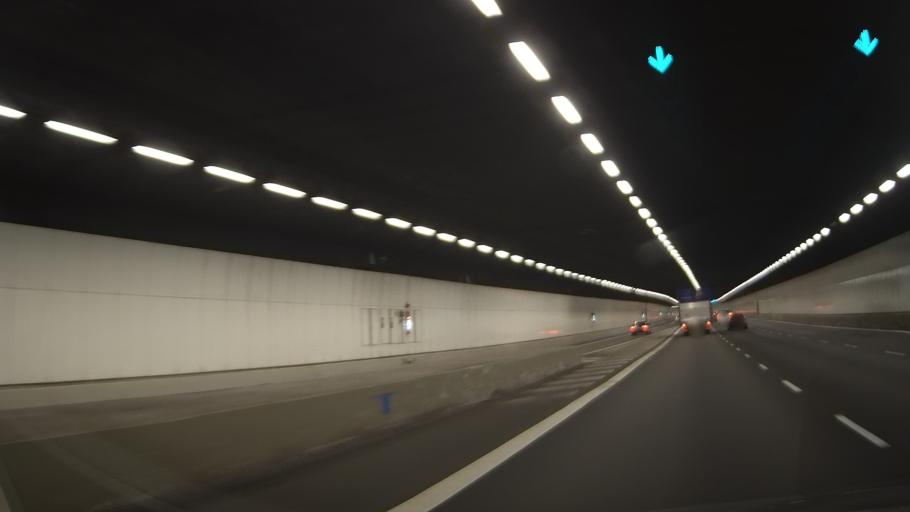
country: SG
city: Singapore
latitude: 1.3004
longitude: 103.8755
